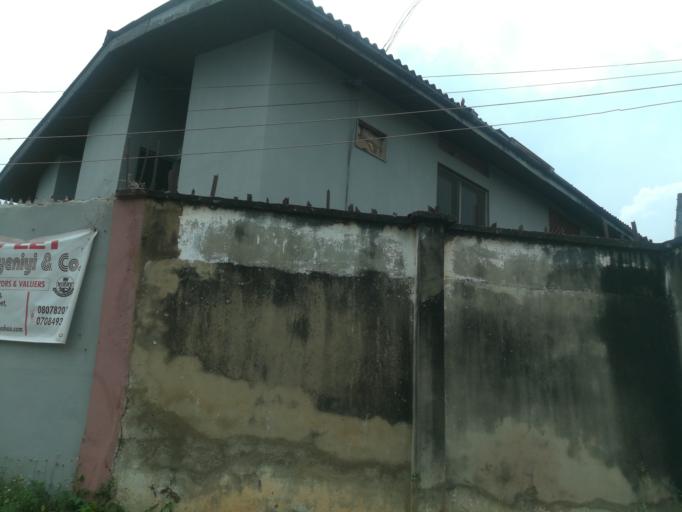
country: NG
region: Oyo
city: Ibadan
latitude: 7.4247
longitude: 3.9201
